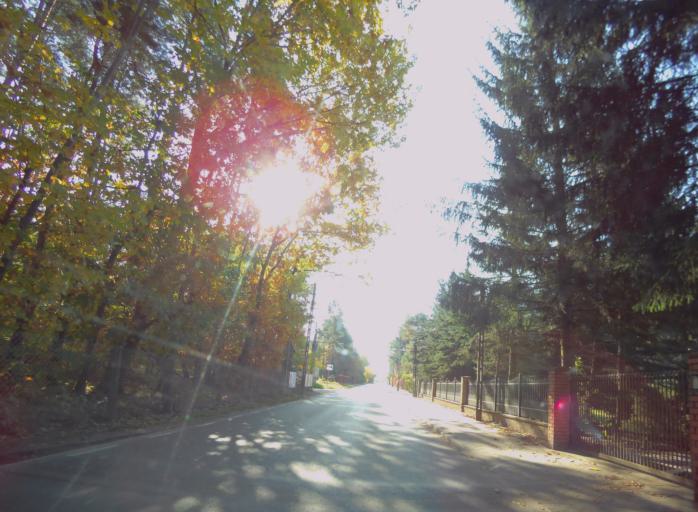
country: PL
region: Masovian Voivodeship
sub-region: Powiat otwocki
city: Jozefow
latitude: 52.1693
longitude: 21.3020
